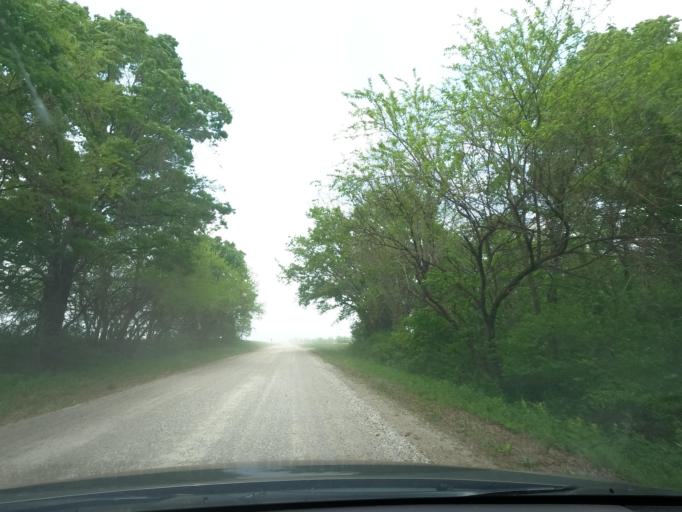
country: US
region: Kansas
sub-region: Labette County
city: Oswego
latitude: 37.3105
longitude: -95.0134
